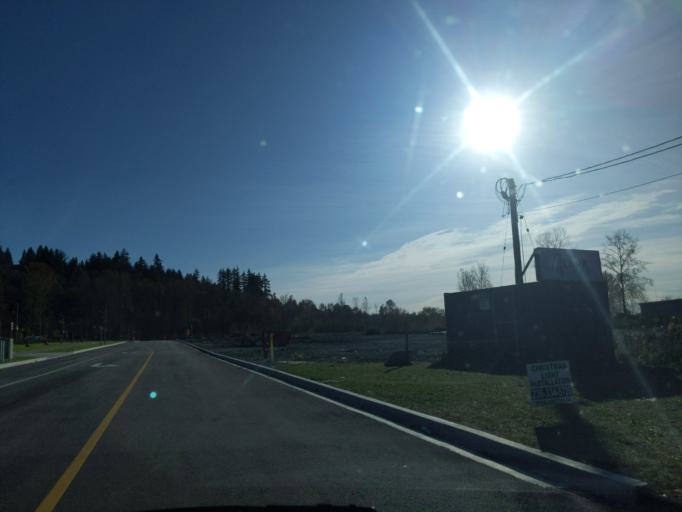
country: CA
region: British Columbia
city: New Westminster
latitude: 49.2025
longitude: -122.8723
